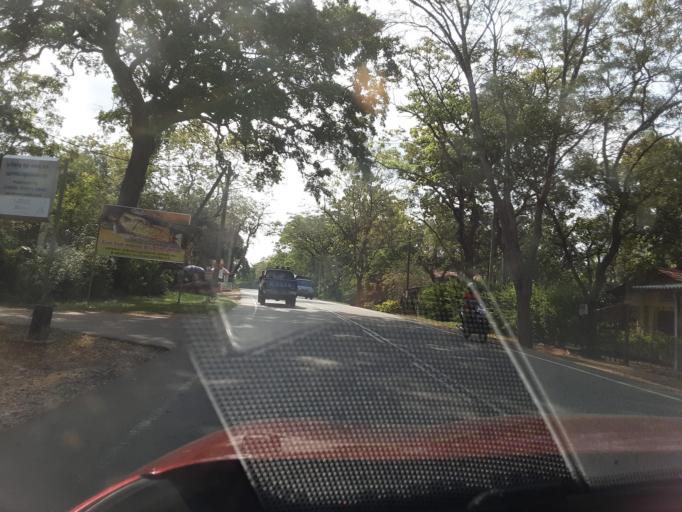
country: LK
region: Uva
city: Haputale
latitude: 6.3558
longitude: 81.1906
